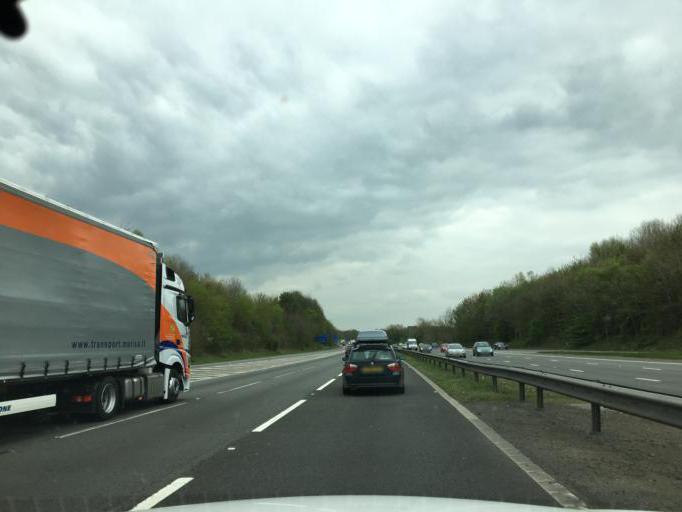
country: GB
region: Wales
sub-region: Rhondda Cynon Taf
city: Llantrisant
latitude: 51.5097
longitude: -3.3539
